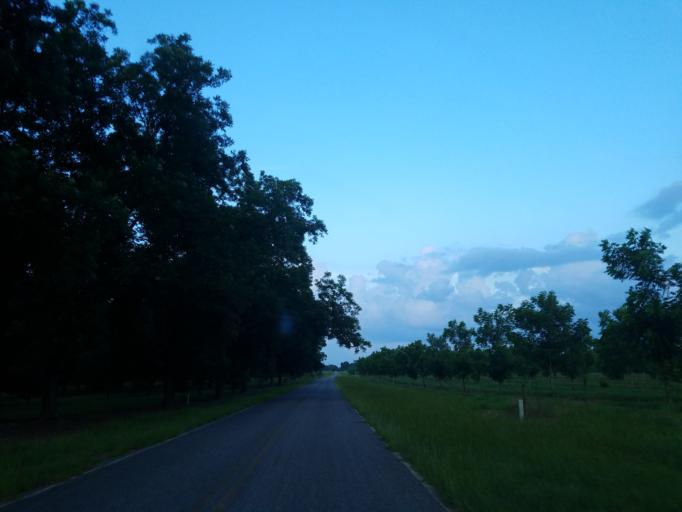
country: US
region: Georgia
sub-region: Dooly County
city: Unadilla
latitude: 32.1753
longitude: -83.7474
